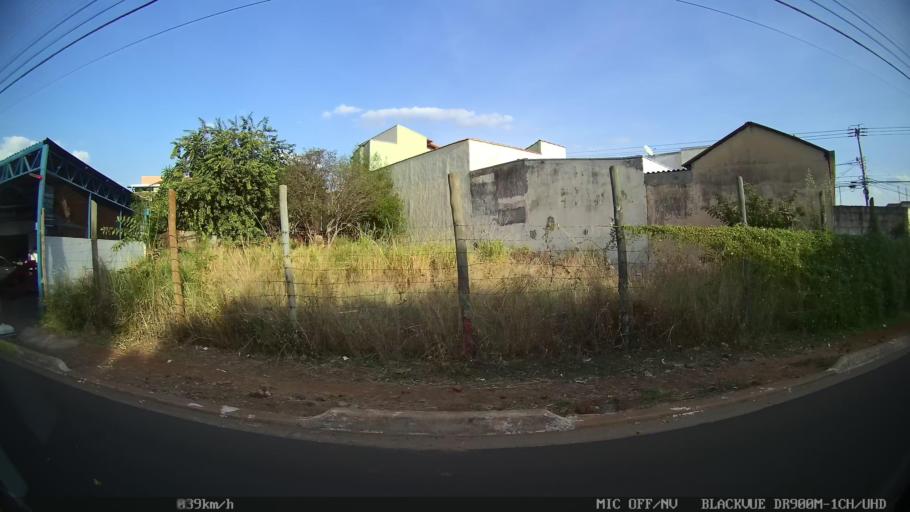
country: BR
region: Sao Paulo
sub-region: Ribeirao Preto
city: Ribeirao Preto
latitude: -21.1660
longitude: -47.8264
